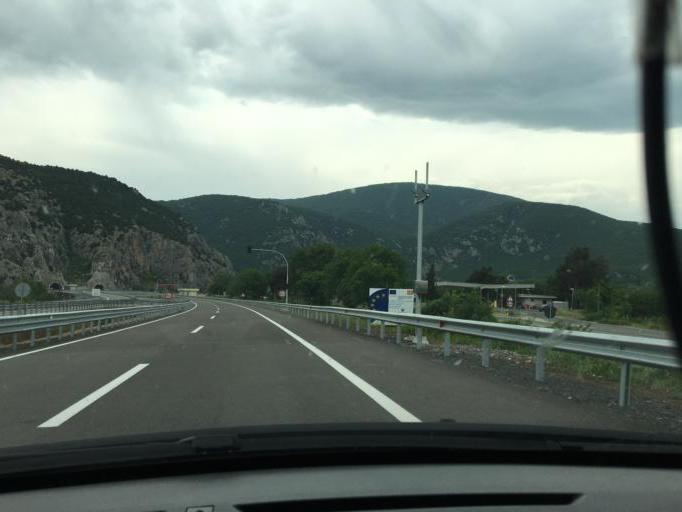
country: MK
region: Demir Kapija
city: Demir Kapija
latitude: 41.4119
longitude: 22.2461
